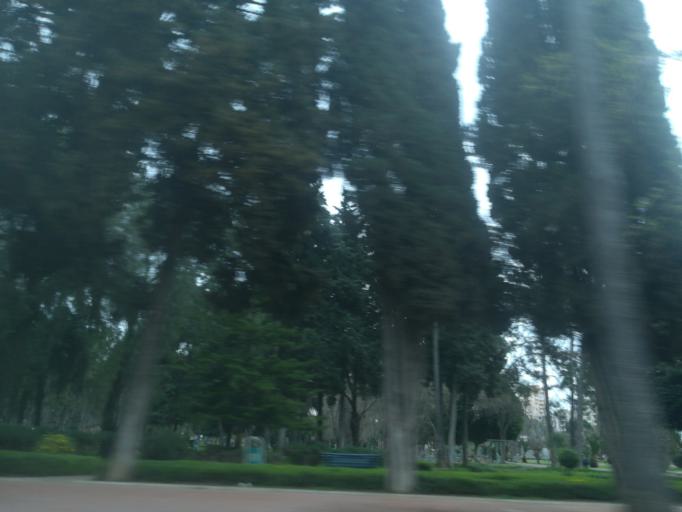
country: TR
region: Adana
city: Adana
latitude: 36.9966
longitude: 35.3216
